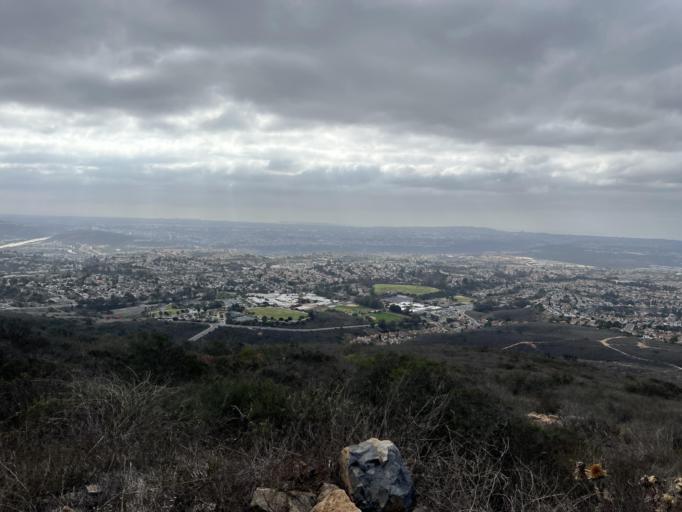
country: US
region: California
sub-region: San Diego County
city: Fairbanks Ranch
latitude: 32.9798
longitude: -117.1165
